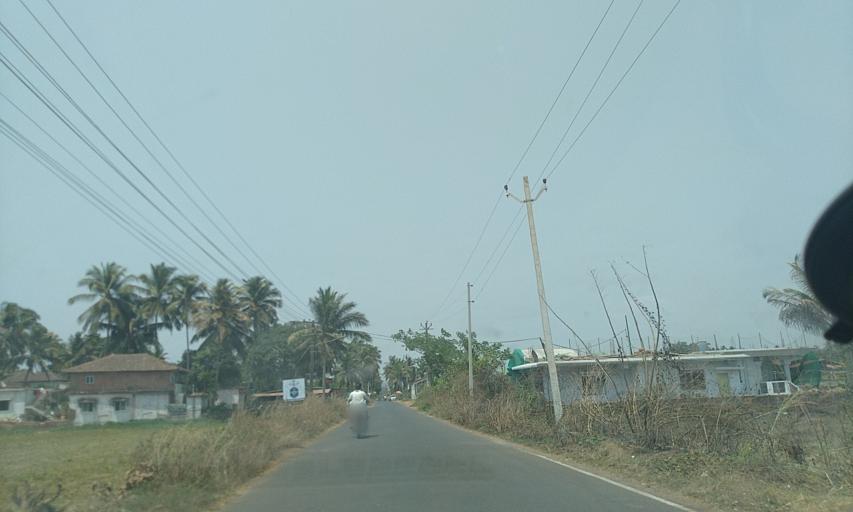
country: IN
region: Goa
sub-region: North Goa
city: Saligao
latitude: 15.5507
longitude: 73.8063
